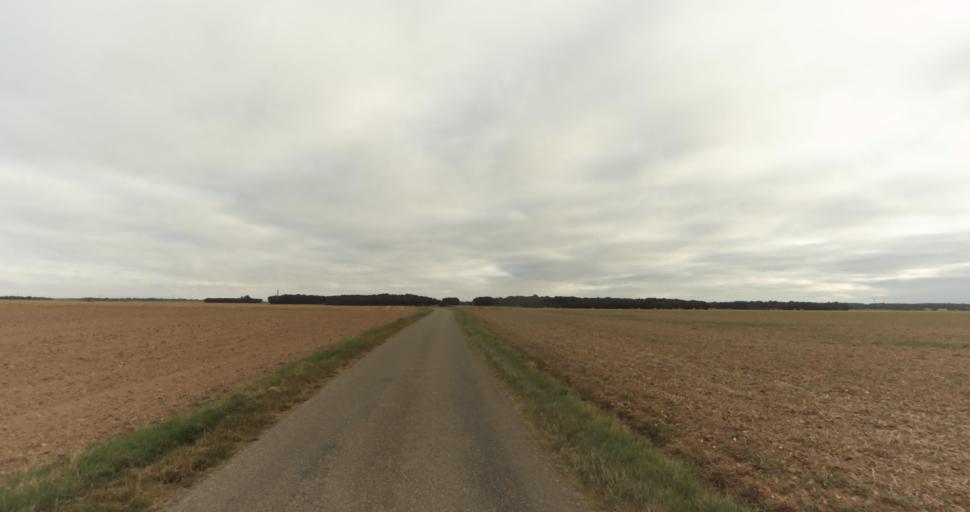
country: FR
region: Haute-Normandie
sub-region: Departement de l'Eure
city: Saint-Germain-sur-Avre
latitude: 48.7862
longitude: 1.2607
